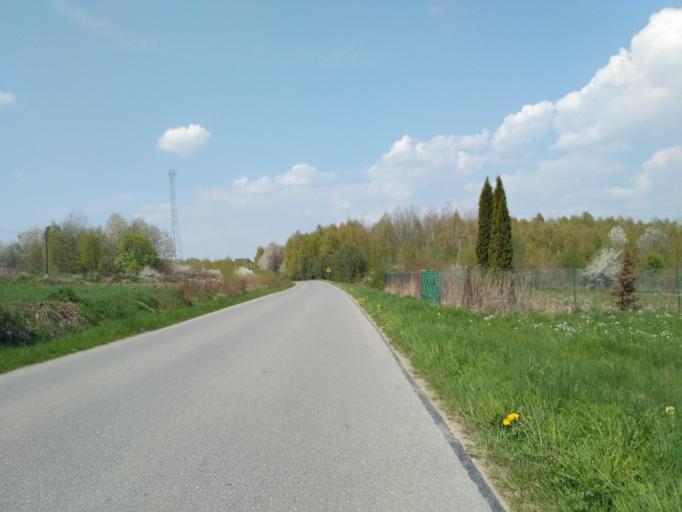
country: PL
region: Subcarpathian Voivodeship
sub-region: Powiat jasielski
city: Osiek Jasielski
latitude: 49.6782
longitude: 21.5152
